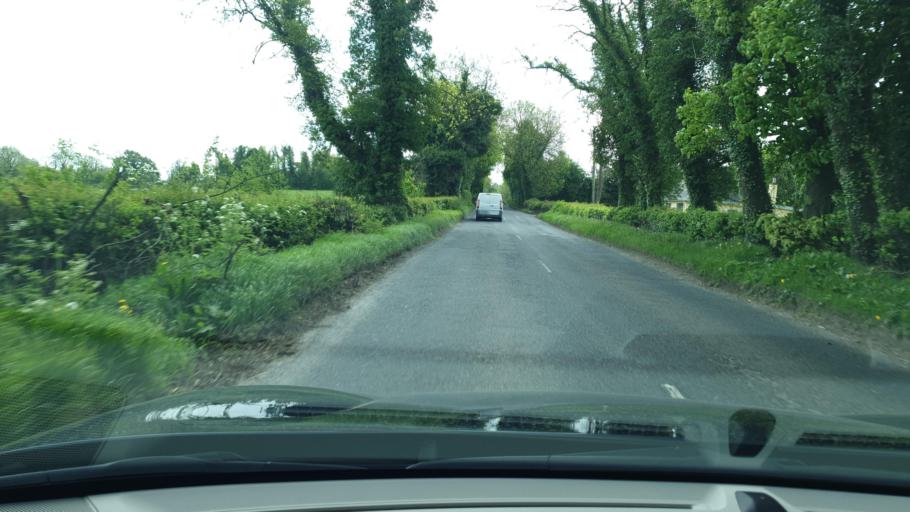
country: IE
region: Ulster
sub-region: An Cabhan
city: Kingscourt
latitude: 53.8348
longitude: -6.7646
